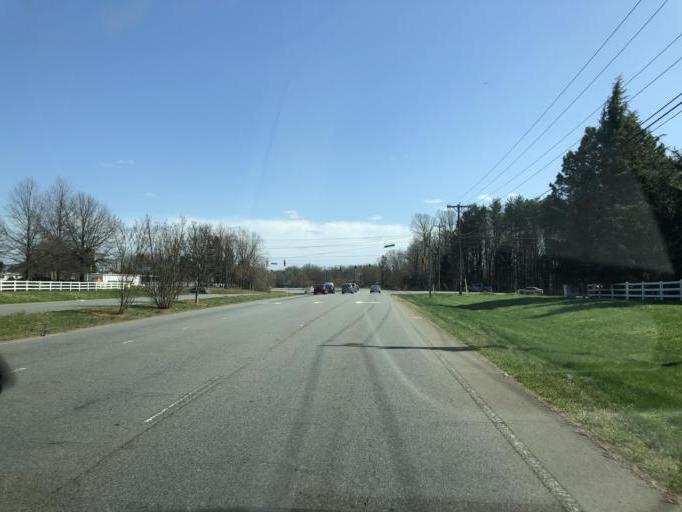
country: US
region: North Carolina
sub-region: Mecklenburg County
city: Huntersville
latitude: 35.3398
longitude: -80.8352
